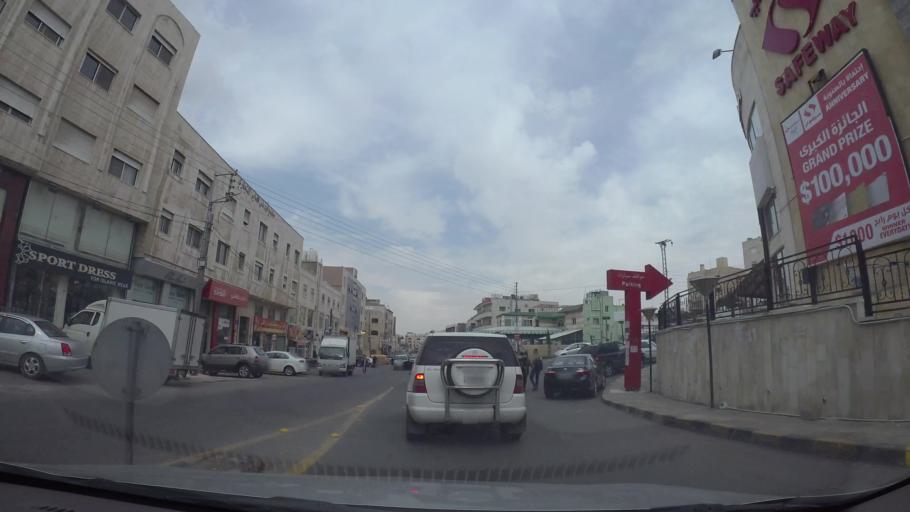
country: JO
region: Amman
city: Umm as Summaq
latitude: 31.8879
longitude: 35.8575
